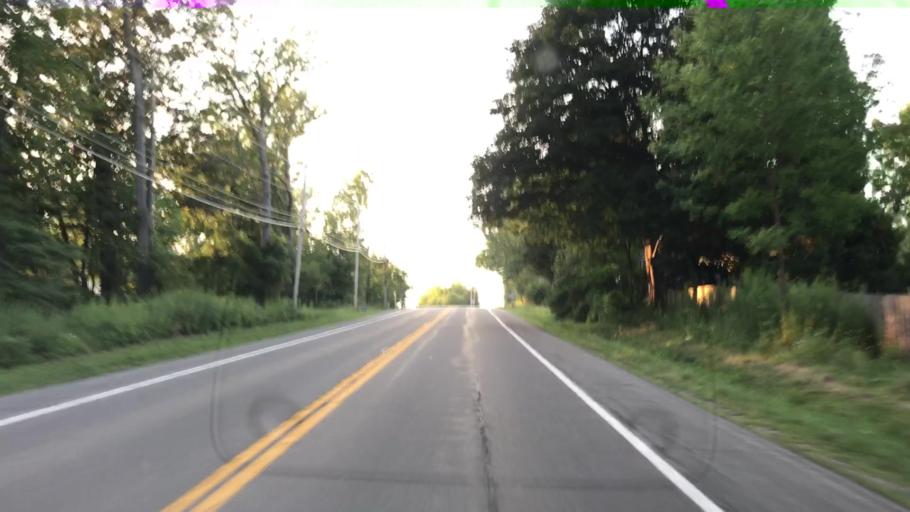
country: US
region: New York
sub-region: Chautauqua County
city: Mayville
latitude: 42.2569
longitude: -79.4678
